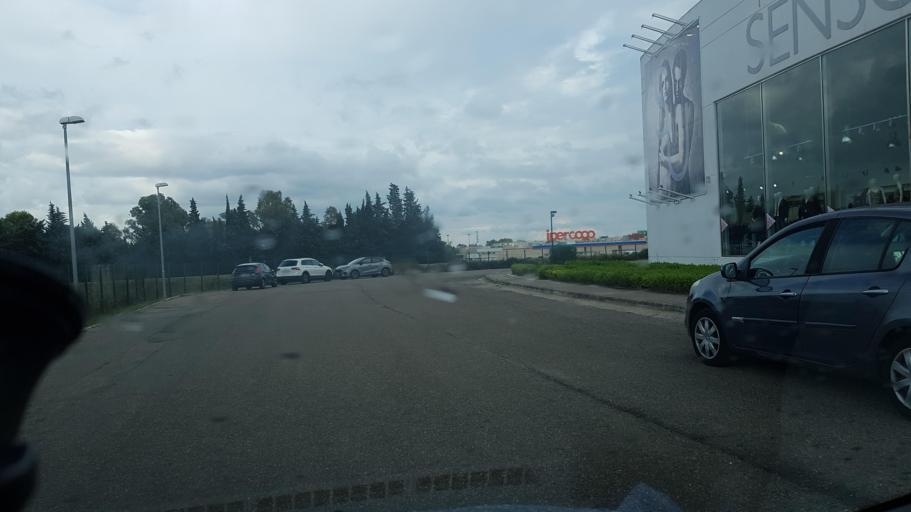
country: IT
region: Apulia
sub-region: Provincia di Lecce
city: Giorgilorio
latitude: 40.3757
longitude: 18.1392
